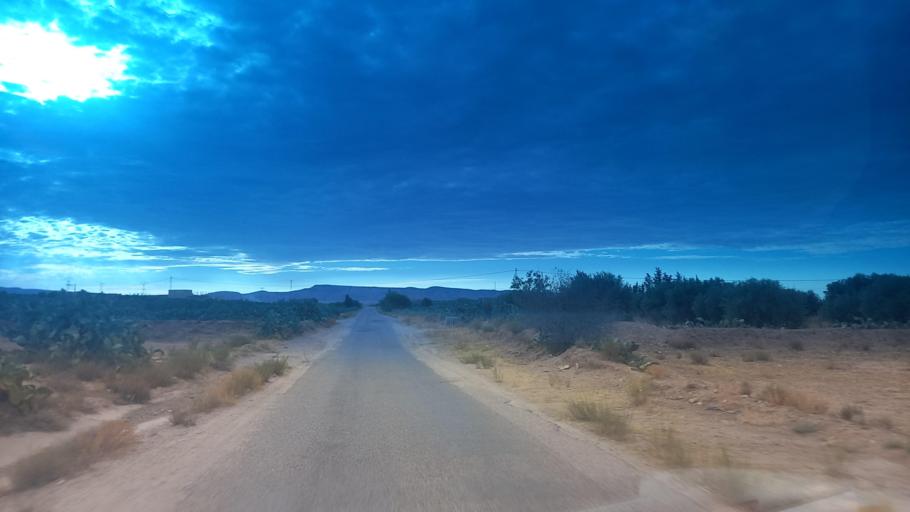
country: TN
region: Al Qasrayn
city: Sbiba
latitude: 35.3848
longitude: 9.0365
